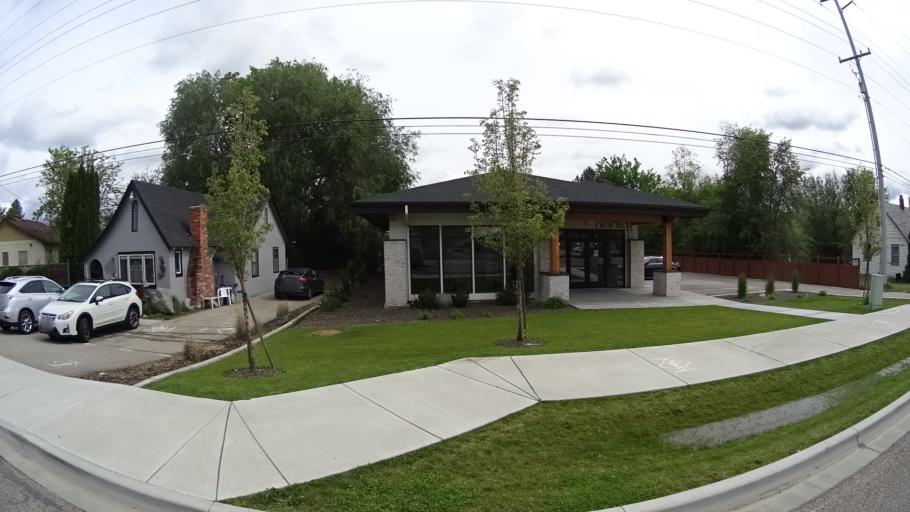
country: US
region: Idaho
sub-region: Ada County
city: Eagle
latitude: 43.6917
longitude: -116.3366
